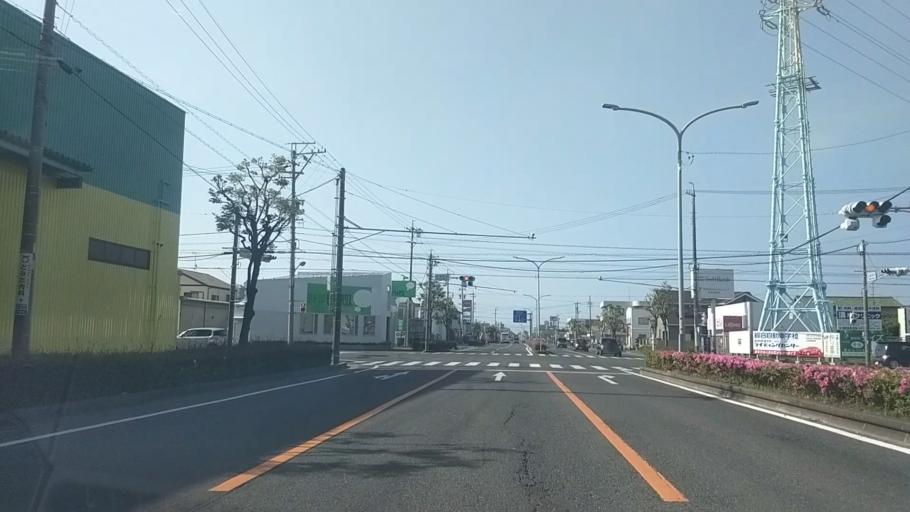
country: JP
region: Shizuoka
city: Hamamatsu
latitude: 34.7032
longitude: 137.7573
